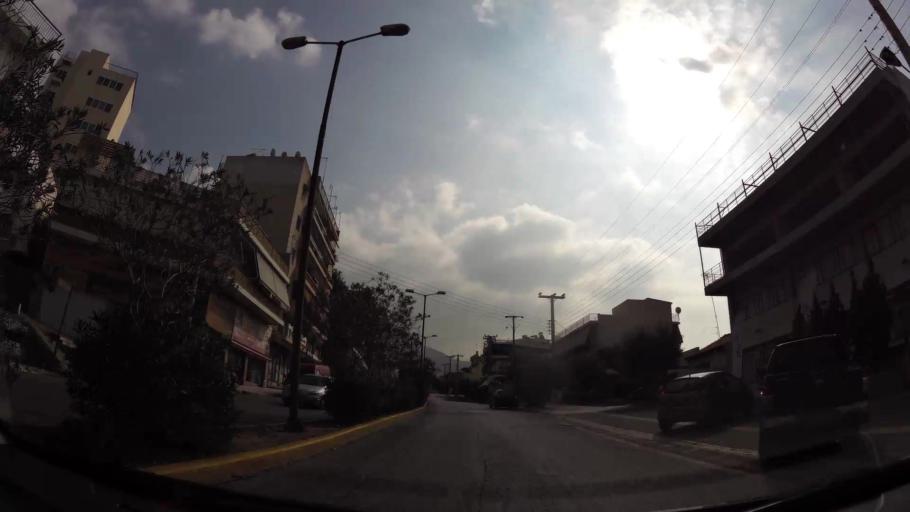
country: GR
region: Attica
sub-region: Nomarchia Athinas
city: Ilioupoli
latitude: 37.9421
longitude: 23.7601
